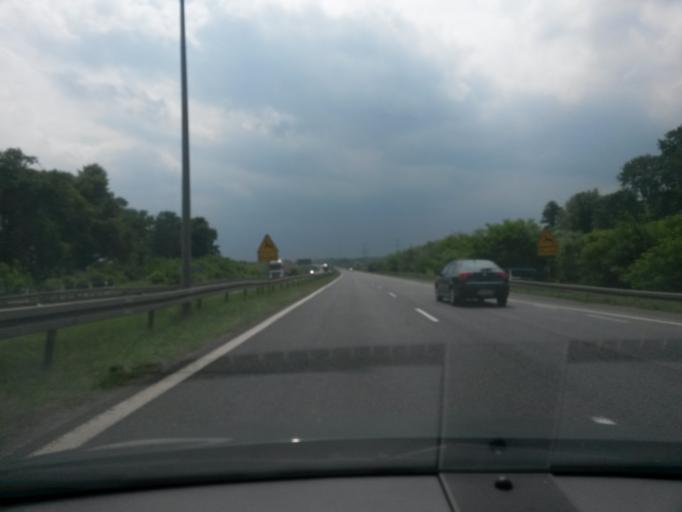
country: PL
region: Lodz Voivodeship
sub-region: Powiat radomszczanski
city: Radomsko
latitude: 51.1063
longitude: 19.3883
